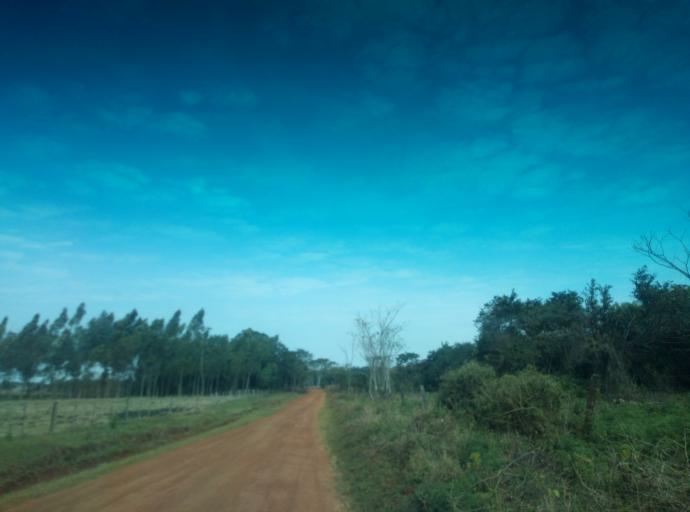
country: PY
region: Caaguazu
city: Carayao
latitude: -25.1956
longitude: -56.2520
